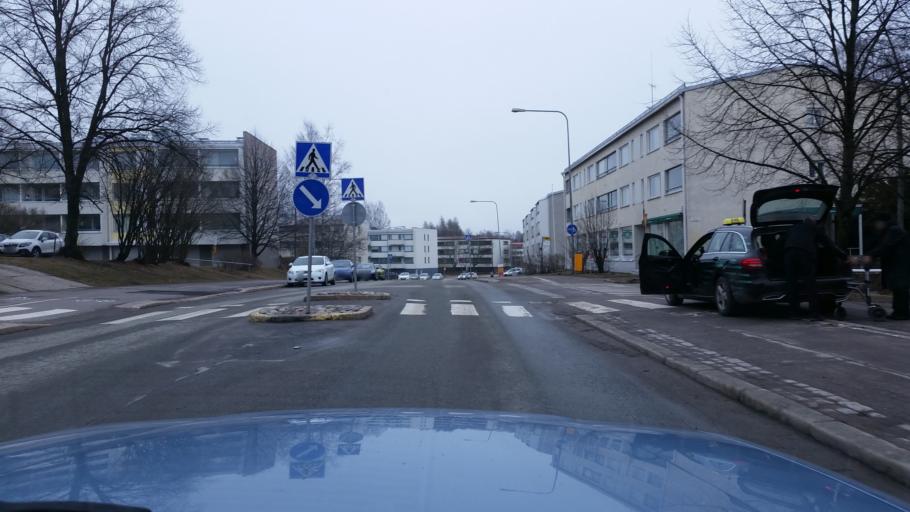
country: FI
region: Uusimaa
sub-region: Helsinki
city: Helsinki
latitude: 60.2271
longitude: 24.9563
